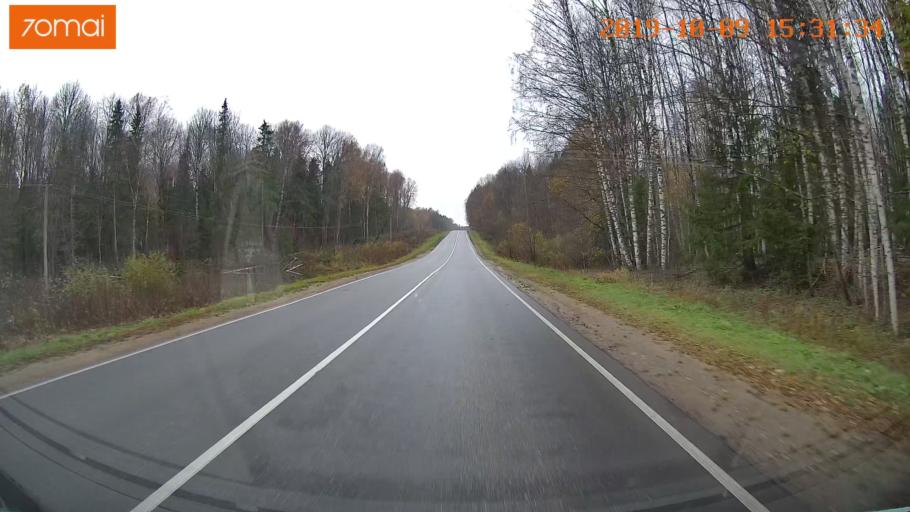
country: RU
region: Kostroma
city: Susanino
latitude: 57.9703
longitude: 41.2990
